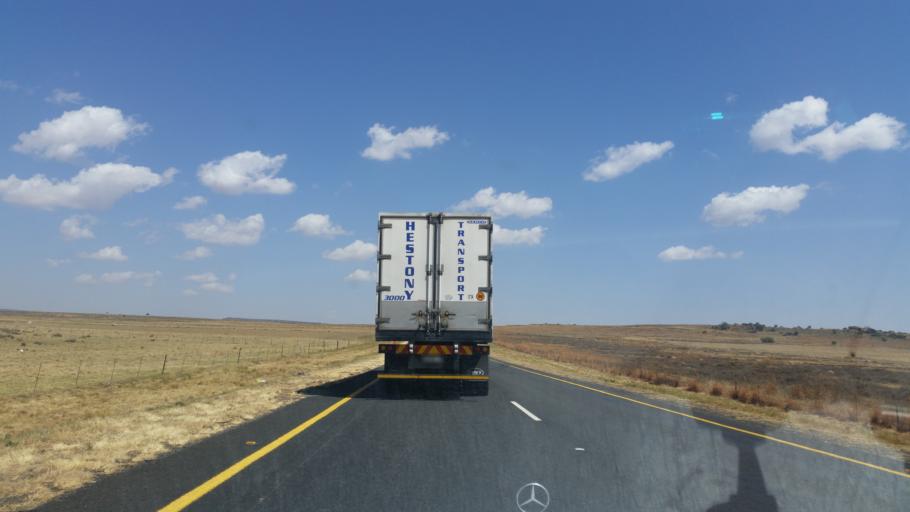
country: ZA
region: Orange Free State
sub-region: Thabo Mofutsanyana District Municipality
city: Senekal
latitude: -28.3104
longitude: 27.8469
